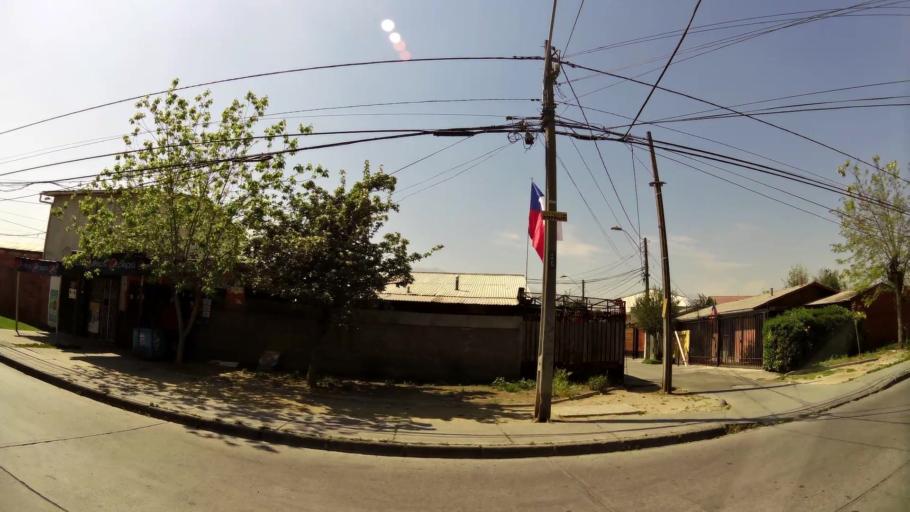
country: CL
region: Santiago Metropolitan
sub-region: Provincia de Santiago
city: La Pintana
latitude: -33.5517
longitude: -70.6061
